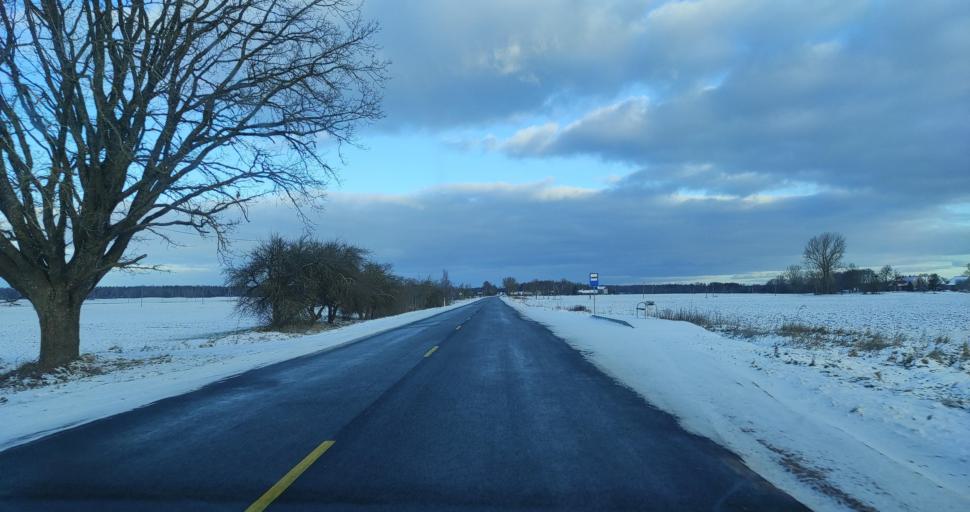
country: LV
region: Skrunda
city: Skrunda
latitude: 56.7002
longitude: 22.0177
